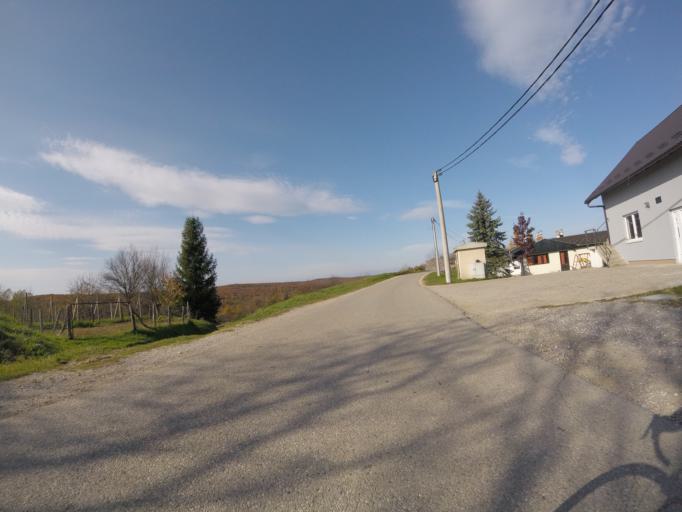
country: HR
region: Zagrebacka
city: Lukavec
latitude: 45.6078
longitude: 16.0043
